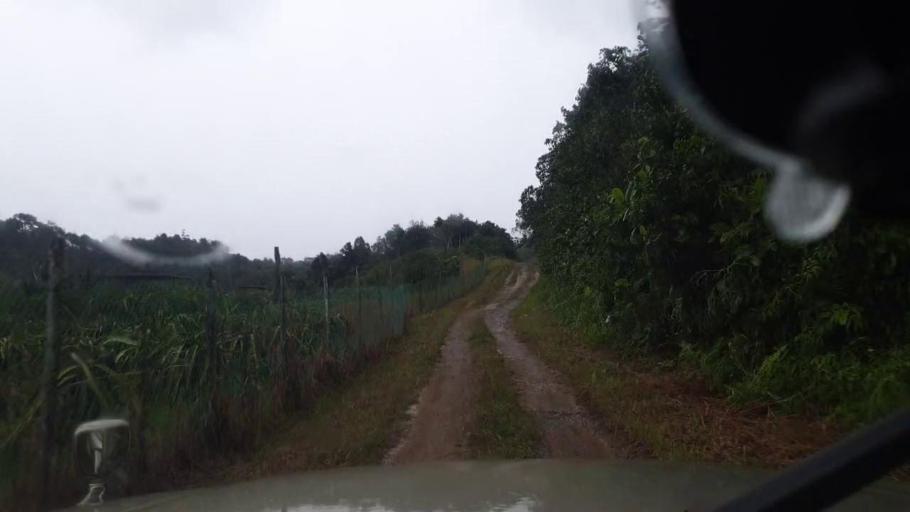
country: MY
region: Sarawak
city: Kuching
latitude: 1.5078
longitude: 110.2345
